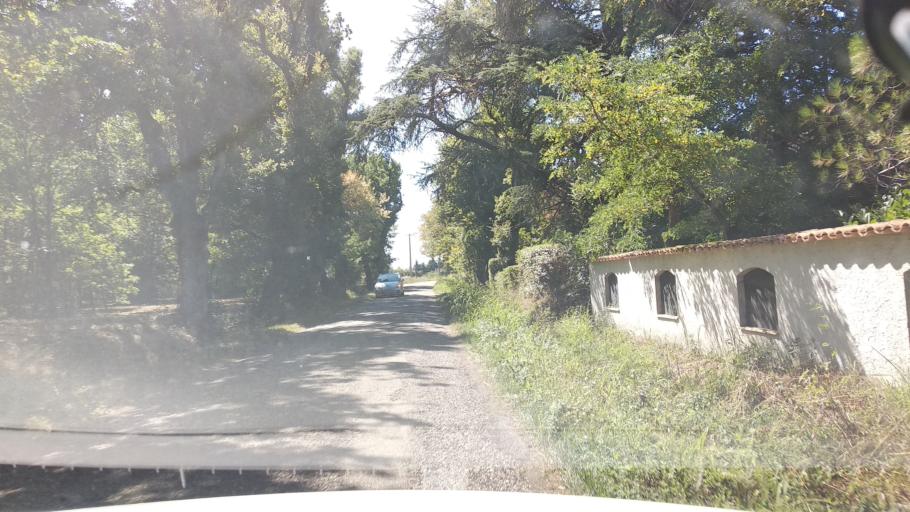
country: FR
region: Midi-Pyrenees
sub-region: Departement du Tarn-et-Garonne
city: Montbeton
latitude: 44.0389
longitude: 1.2453
